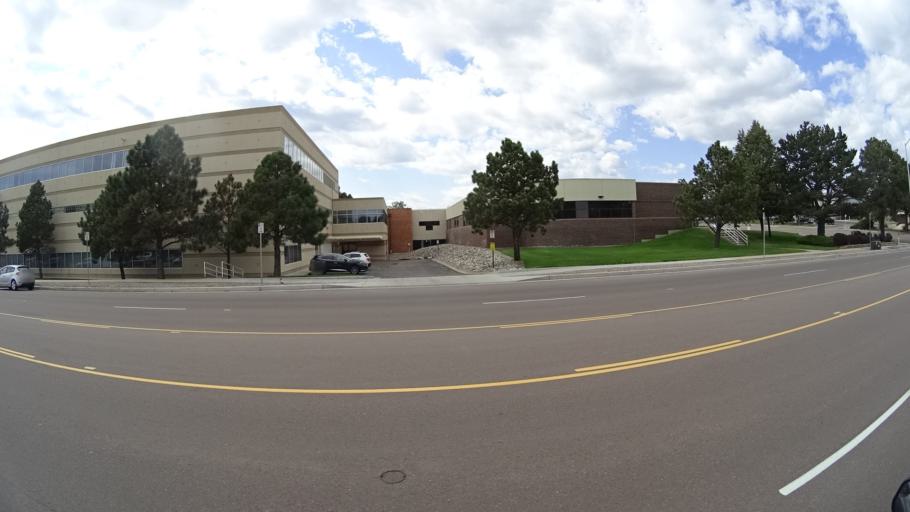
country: US
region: Colorado
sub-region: El Paso County
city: Cimarron Hills
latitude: 38.8787
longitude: -104.7547
